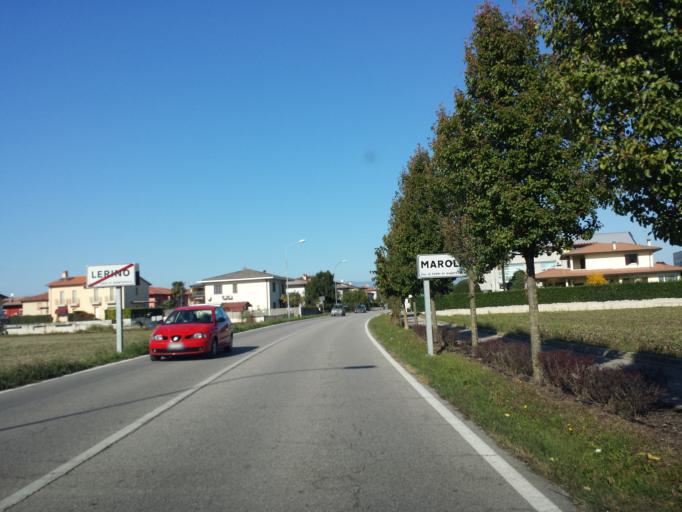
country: IT
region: Veneto
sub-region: Provincia di Vicenza
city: Marola
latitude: 45.5293
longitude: 11.6314
